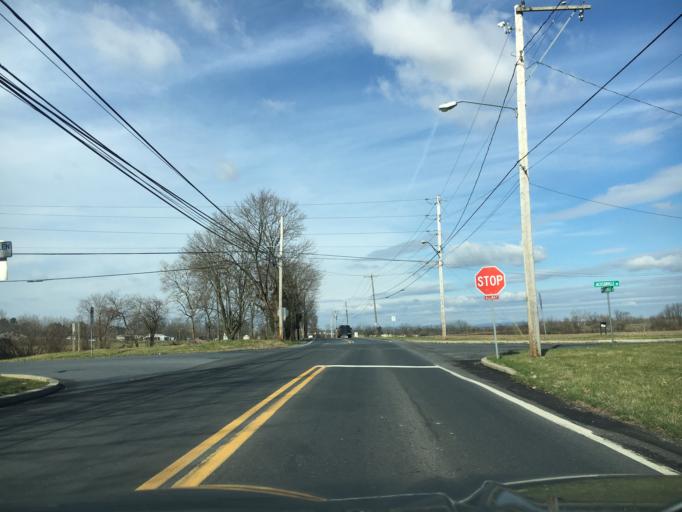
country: US
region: Pennsylvania
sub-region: Northampton County
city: Bath
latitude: 40.6825
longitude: -75.4092
